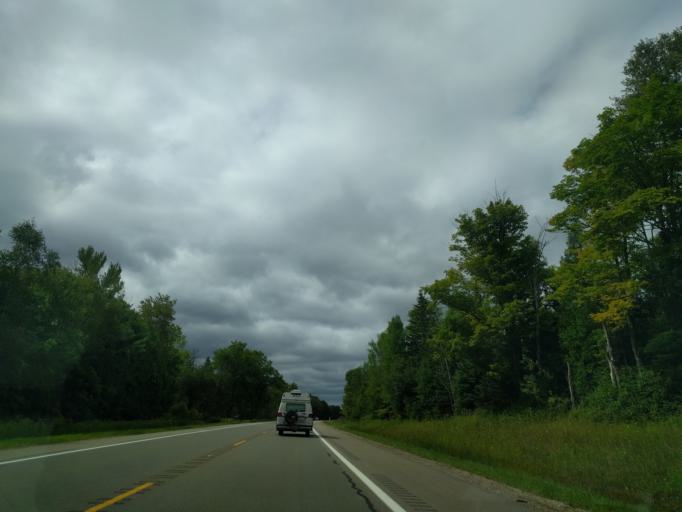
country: US
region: Michigan
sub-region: Menominee County
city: Menominee
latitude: 45.2647
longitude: -87.4730
